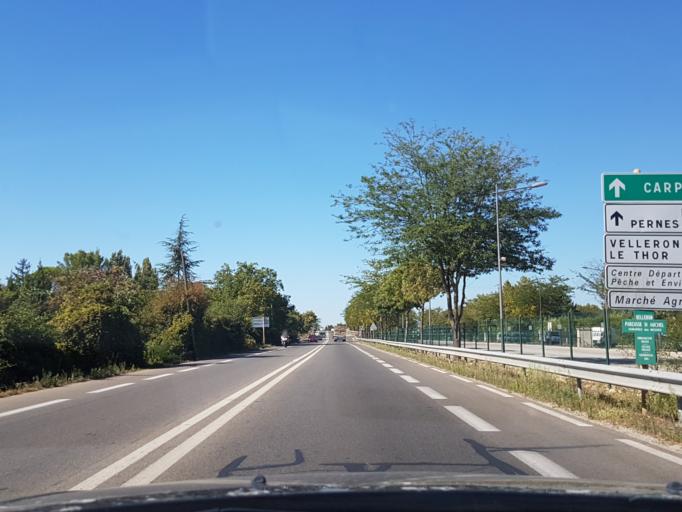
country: FR
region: Provence-Alpes-Cote d'Azur
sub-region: Departement du Vaucluse
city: Velleron
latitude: 43.9525
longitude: 5.0268
